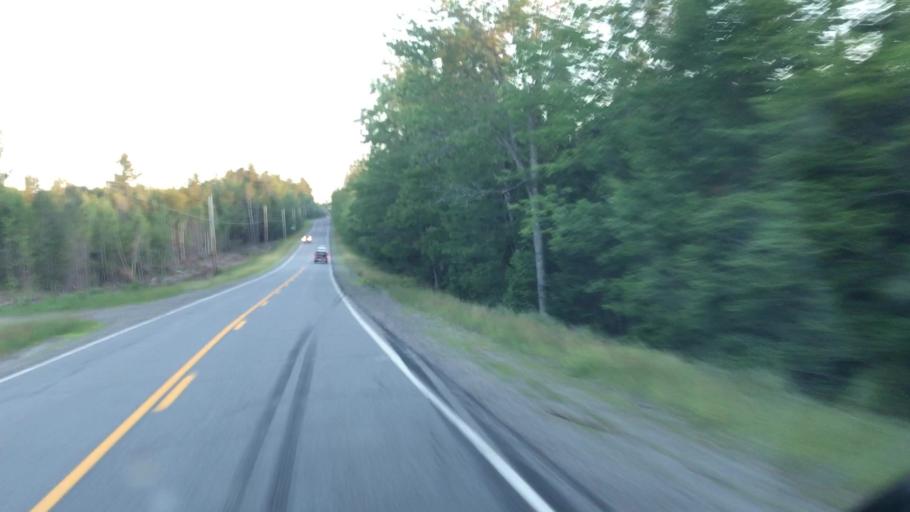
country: US
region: Maine
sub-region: Penobscot County
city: Medway
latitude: 45.5907
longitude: -68.3131
